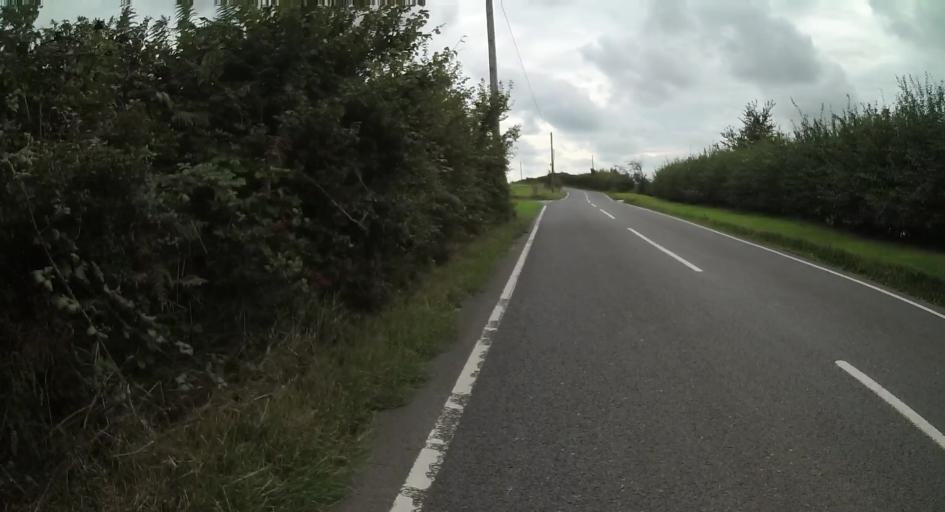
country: GB
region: England
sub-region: Isle of Wight
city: Niton
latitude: 50.6177
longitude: -1.2646
